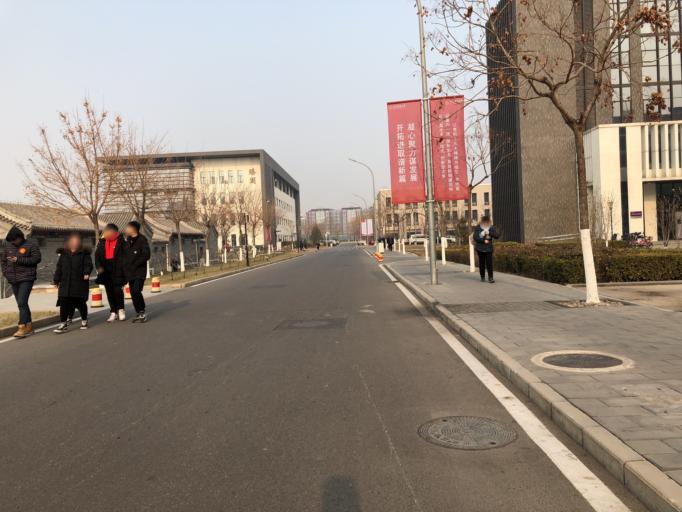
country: CN
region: Beijing
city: Daxing
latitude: 39.7460
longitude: 116.2824
